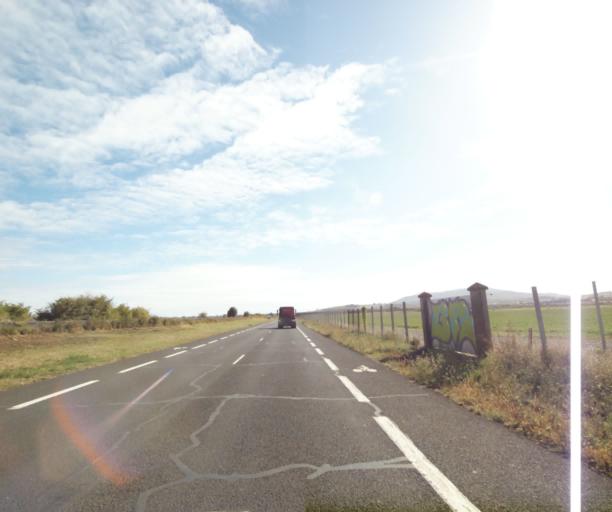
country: FR
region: Auvergne
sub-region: Departement du Puy-de-Dome
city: Malintrat
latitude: 45.7905
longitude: 3.1908
